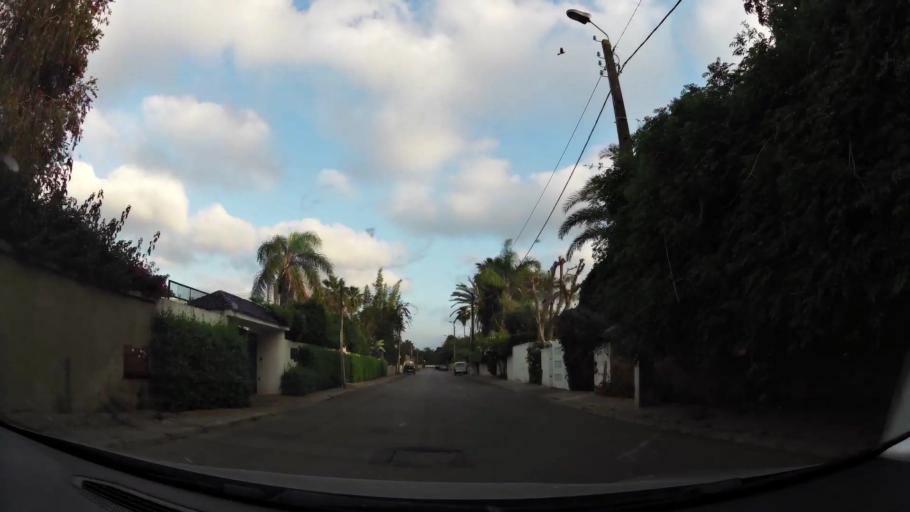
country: MA
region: Rabat-Sale-Zemmour-Zaer
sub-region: Rabat
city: Rabat
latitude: 33.9615
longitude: -6.8314
